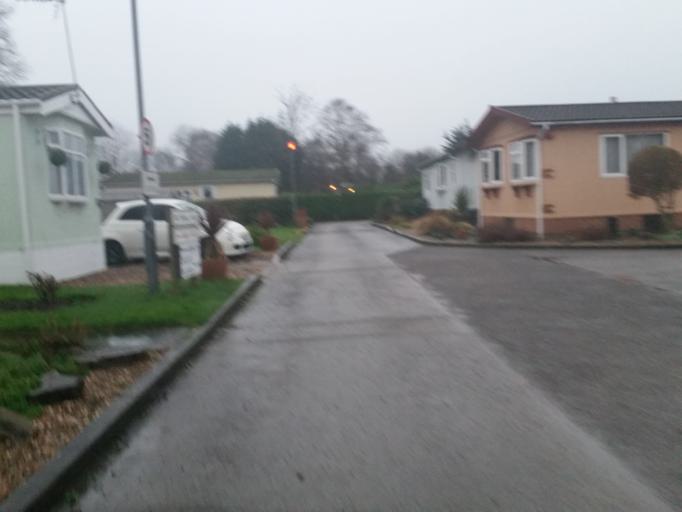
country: GB
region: England
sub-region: Derby
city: Derby
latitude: 52.9031
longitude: -1.4353
